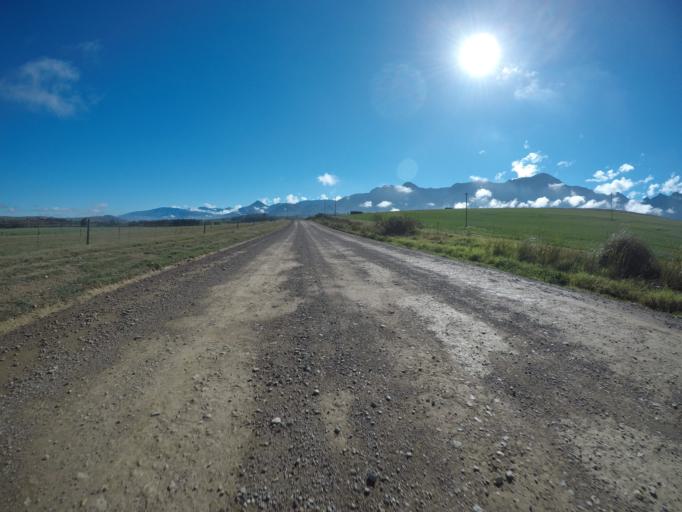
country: ZA
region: Western Cape
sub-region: Overberg District Municipality
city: Caledon
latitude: -34.1056
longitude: 19.7052
